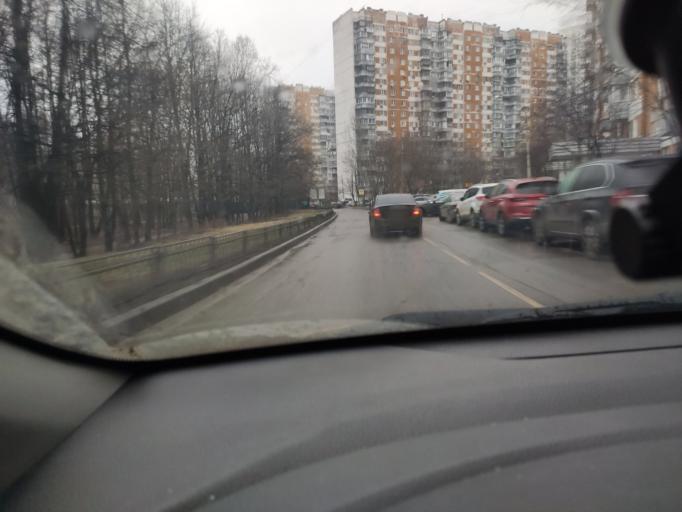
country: RU
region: Moscow
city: Chertanovo Yuzhnoye
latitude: 55.5929
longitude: 37.5931
